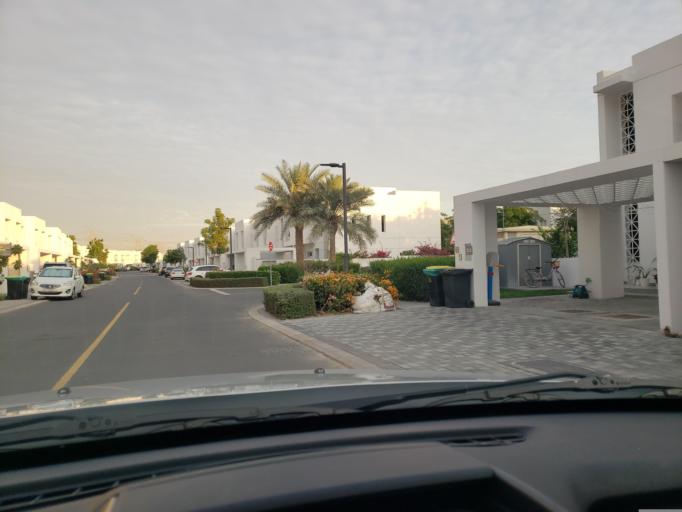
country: AE
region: Dubai
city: Dubai
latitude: 25.0177
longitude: 55.2714
